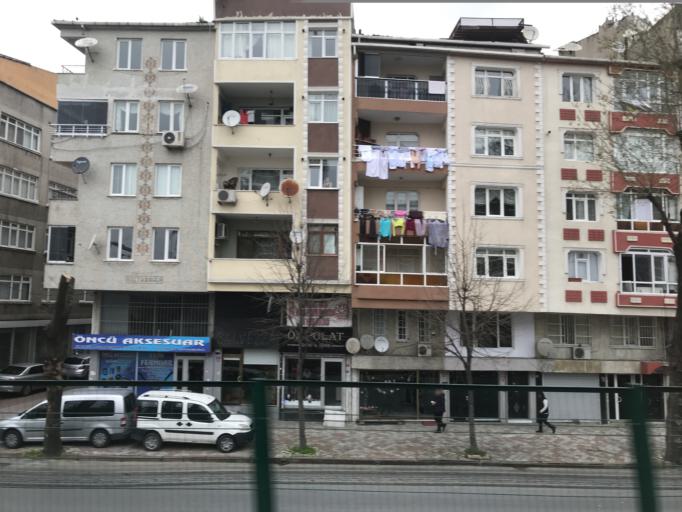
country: TR
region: Istanbul
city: Zeytinburnu
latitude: 40.9832
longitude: 28.9011
